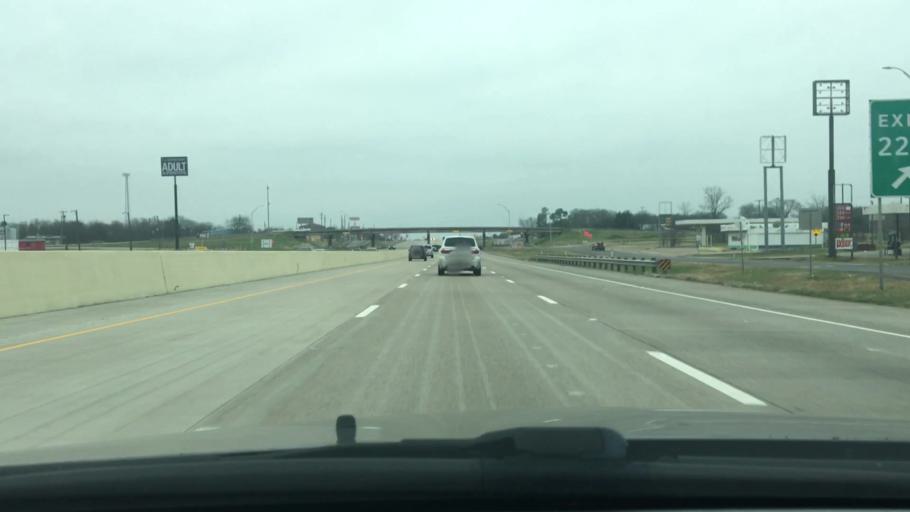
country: US
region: Texas
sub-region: Navarro County
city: Corsicana
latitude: 32.0113
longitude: -96.4352
